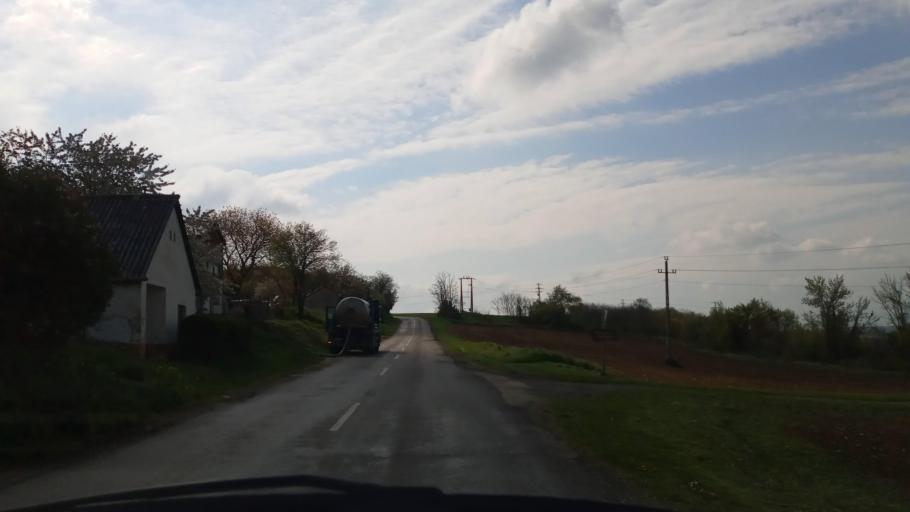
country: HU
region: Baranya
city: Pecsvarad
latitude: 46.1567
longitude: 18.4357
